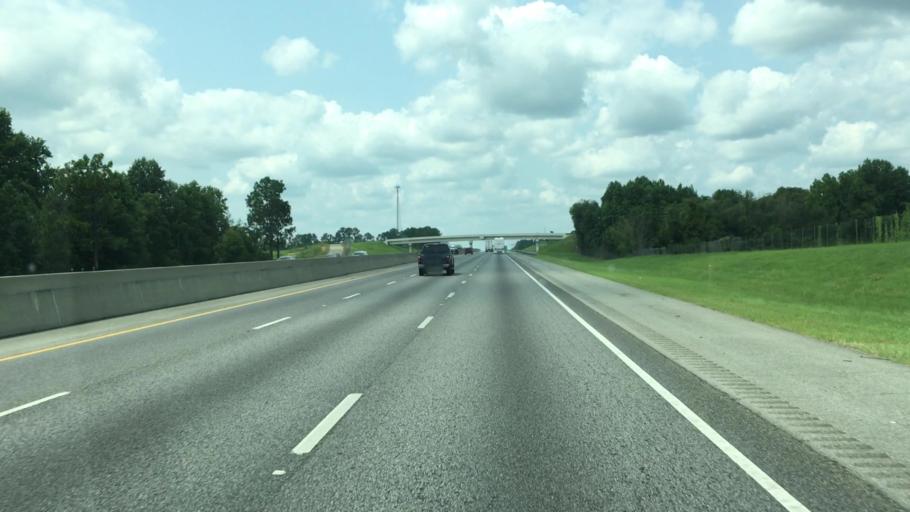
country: US
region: Georgia
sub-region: Turner County
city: Ashburn
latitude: 31.6431
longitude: -83.5895
